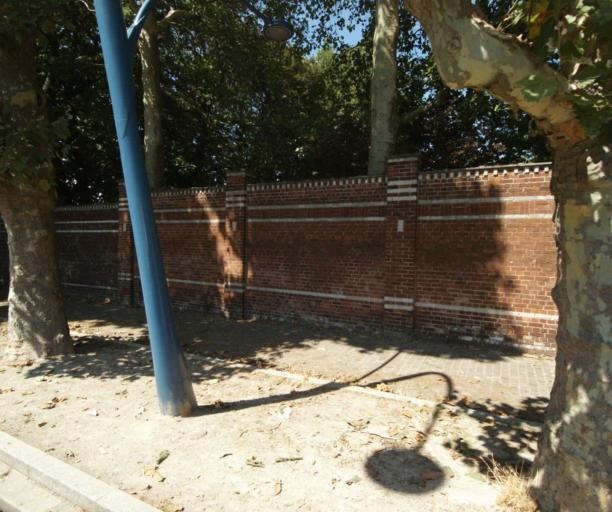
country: FR
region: Nord-Pas-de-Calais
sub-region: Departement du Nord
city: Halluin
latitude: 50.7828
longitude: 3.1234
